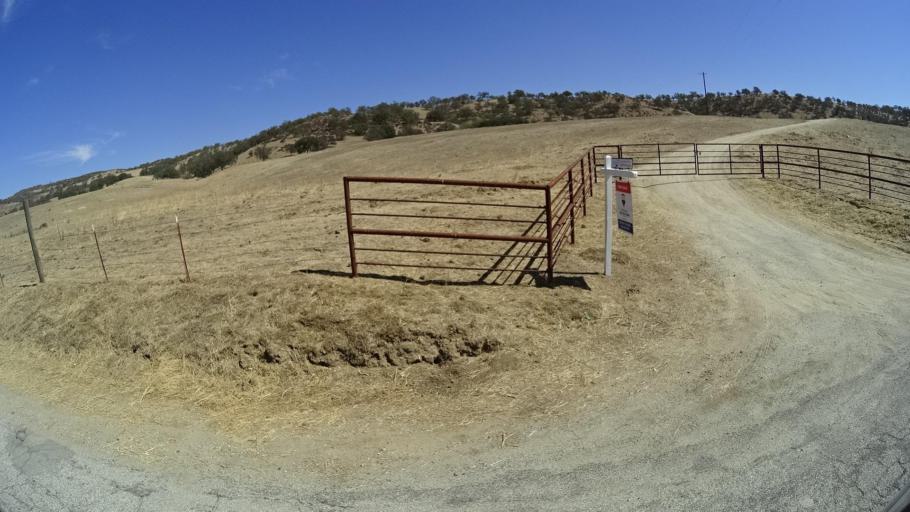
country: US
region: California
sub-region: San Luis Obispo County
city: San Miguel
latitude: 35.8878
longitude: -120.7015
